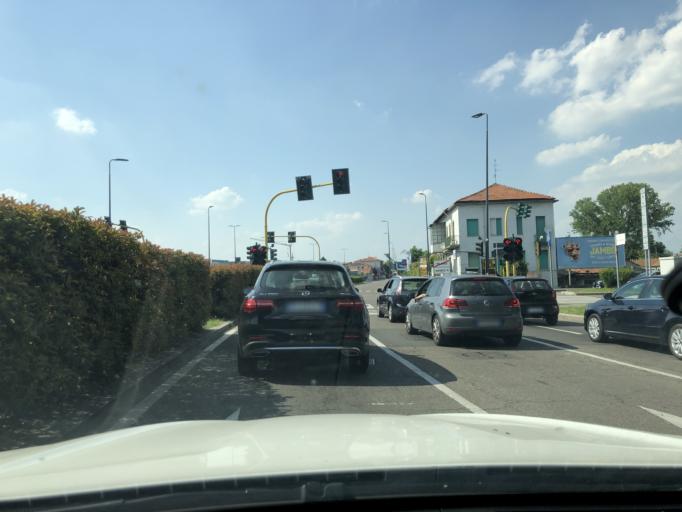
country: IT
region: Lombardy
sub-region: Citta metropolitana di Milano
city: Novate Milanese
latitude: 45.5207
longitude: 9.1513
